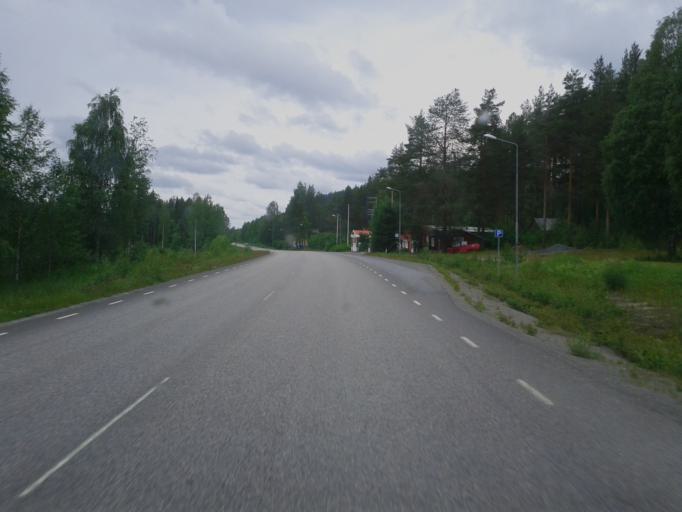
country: SE
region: Vaesterbotten
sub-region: Skelleftea Kommun
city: Langsele
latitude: 64.9166
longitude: 20.0987
